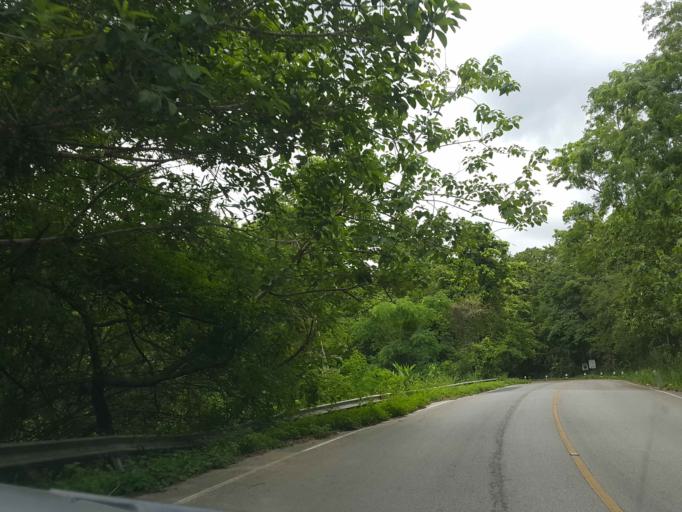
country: TH
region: Chiang Mai
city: Hang Dong
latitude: 18.7802
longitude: 98.8513
